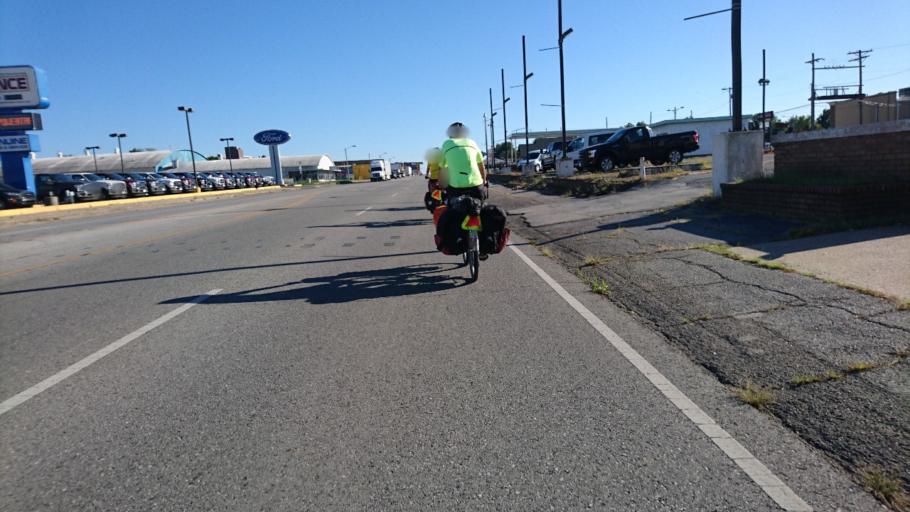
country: US
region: Oklahoma
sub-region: Ottawa County
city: Miami
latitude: 36.8827
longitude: -94.8777
